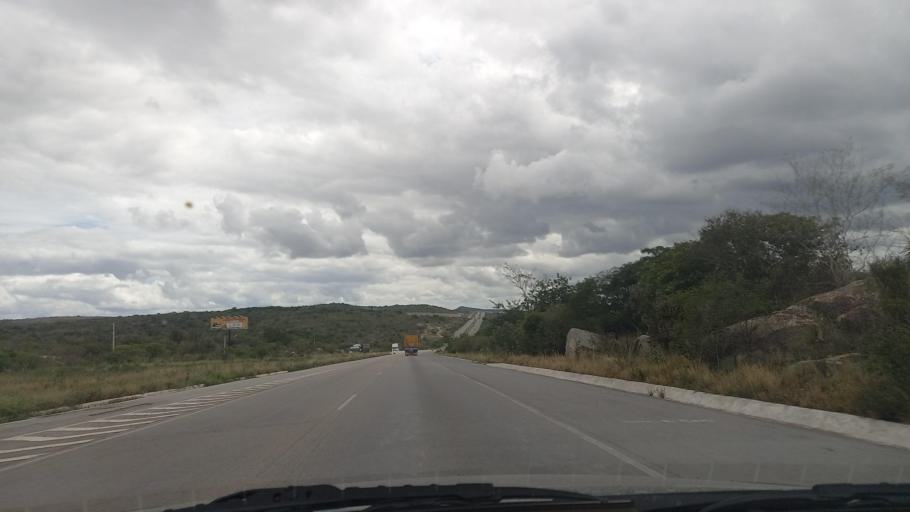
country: BR
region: Pernambuco
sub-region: Caruaru
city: Caruaru
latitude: -8.3213
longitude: -36.0873
